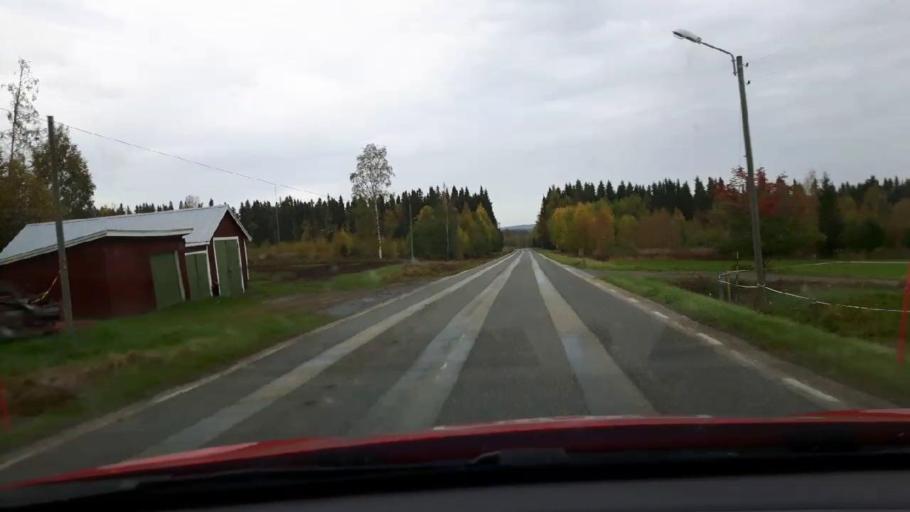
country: SE
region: Jaemtland
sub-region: Bergs Kommun
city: Hoverberg
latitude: 62.8614
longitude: 14.3774
